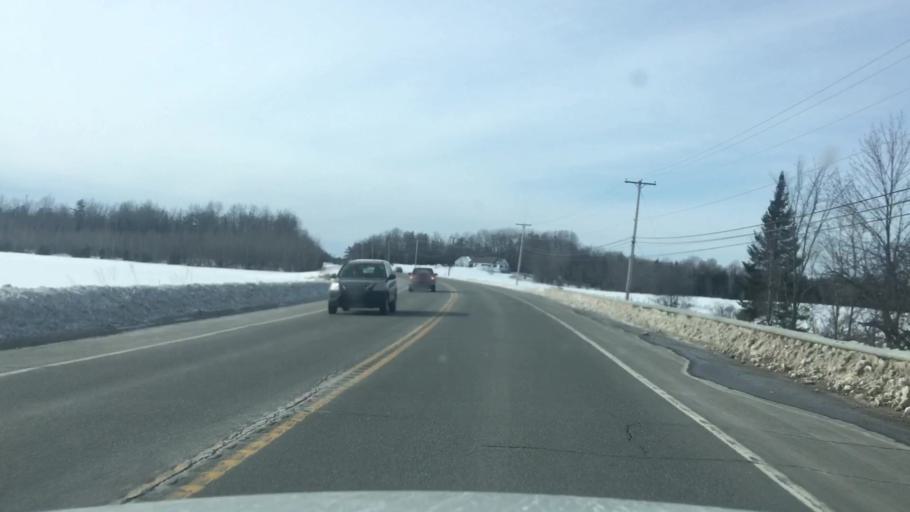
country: US
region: Maine
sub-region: Penobscot County
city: Kenduskeag
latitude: 44.9107
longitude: -68.8988
